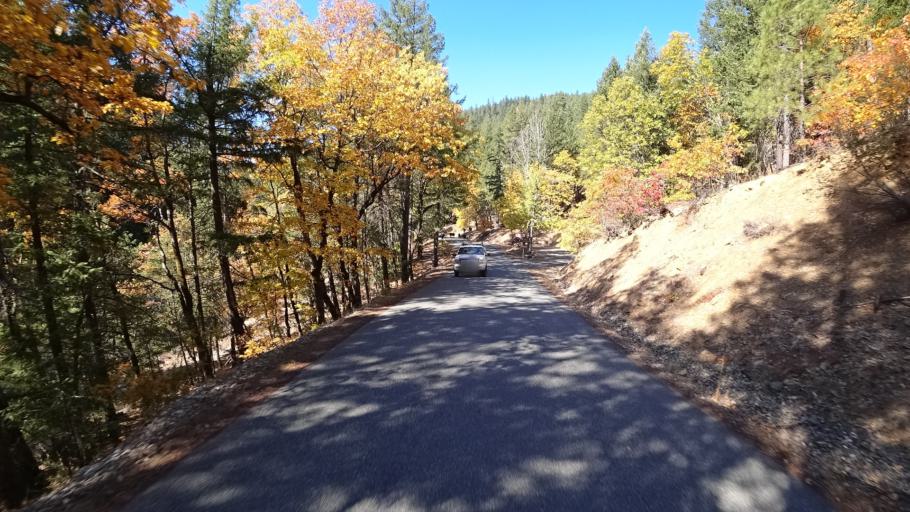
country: US
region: California
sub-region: Siskiyou County
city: Happy Camp
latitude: 41.6398
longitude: -123.0594
